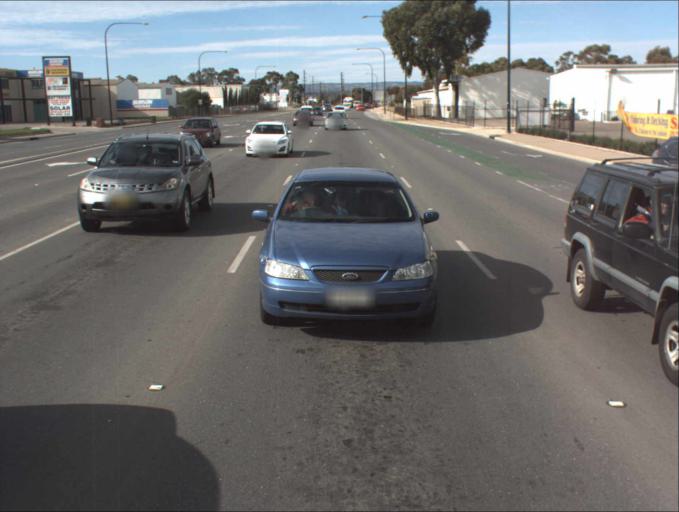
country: AU
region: South Australia
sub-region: Charles Sturt
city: Woodville North
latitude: -34.8498
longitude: 138.5650
